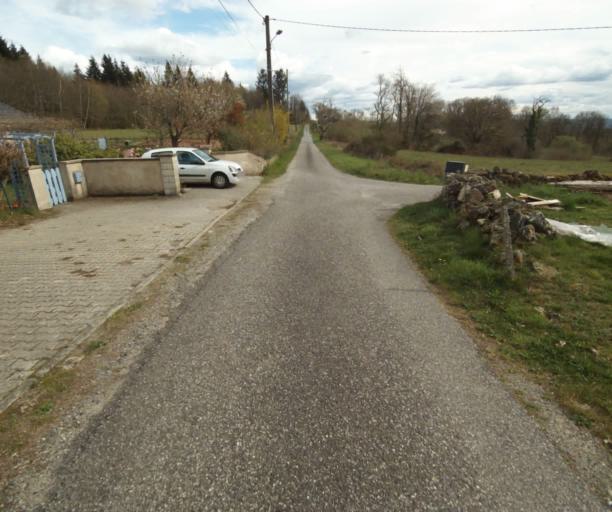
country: FR
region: Limousin
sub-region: Departement de la Correze
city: Argentat
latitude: 45.1939
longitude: 1.9489
